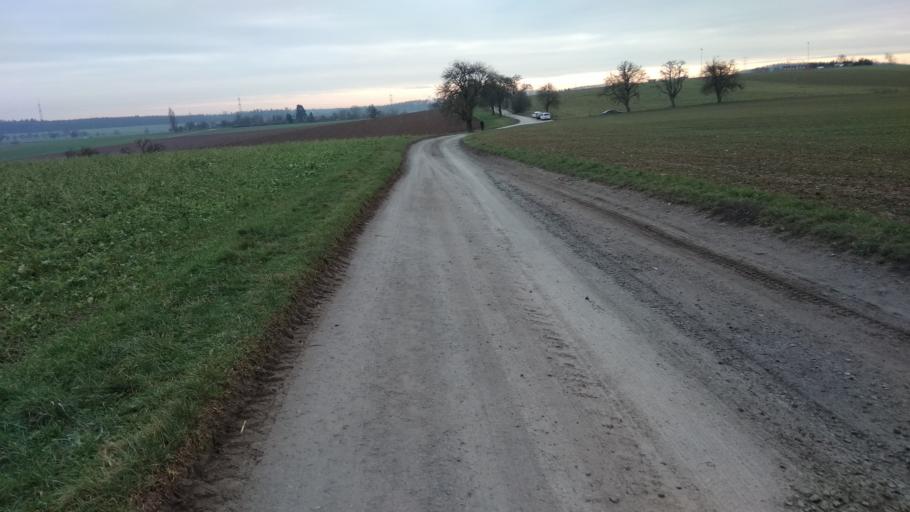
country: DE
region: Baden-Wuerttemberg
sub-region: Karlsruhe Region
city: Mosbach
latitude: 49.3534
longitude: 9.1765
